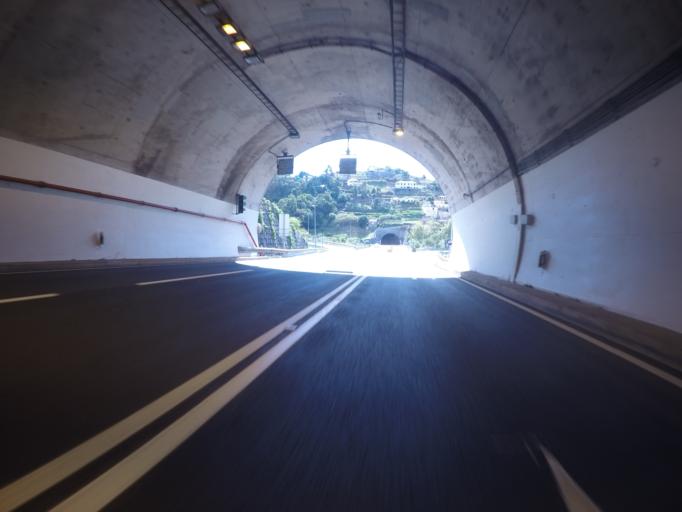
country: PT
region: Madeira
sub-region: Santa Cruz
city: Camacha
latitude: 32.6596
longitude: -16.8508
